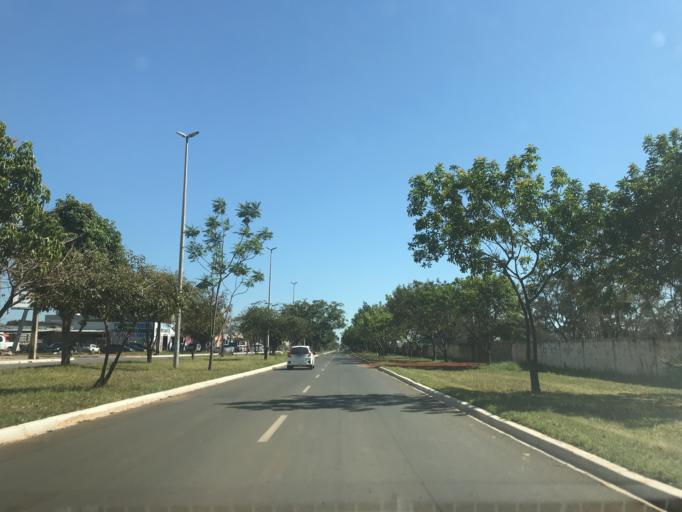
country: BR
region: Federal District
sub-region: Brasilia
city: Brasilia
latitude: -15.8068
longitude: -48.0896
